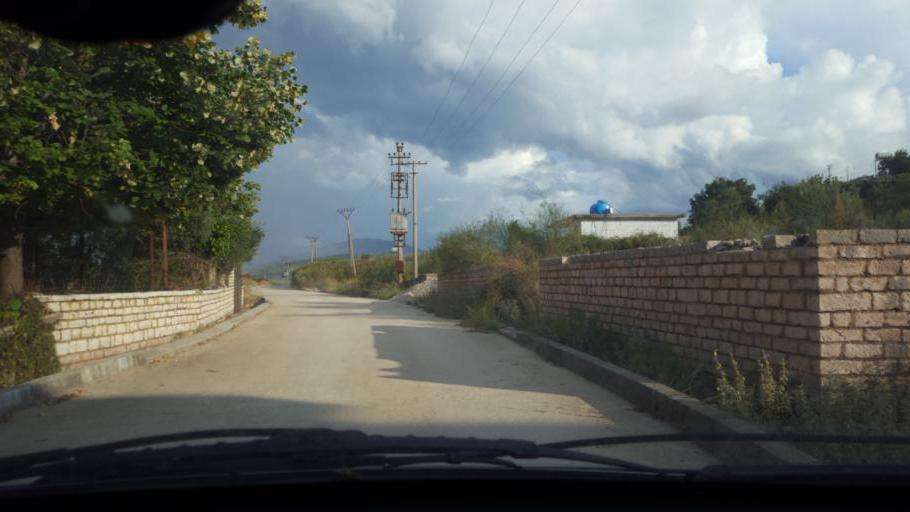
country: AL
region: Vlore
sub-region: Rrethi i Sarandes
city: Sarande
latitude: 39.8408
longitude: 20.0215
